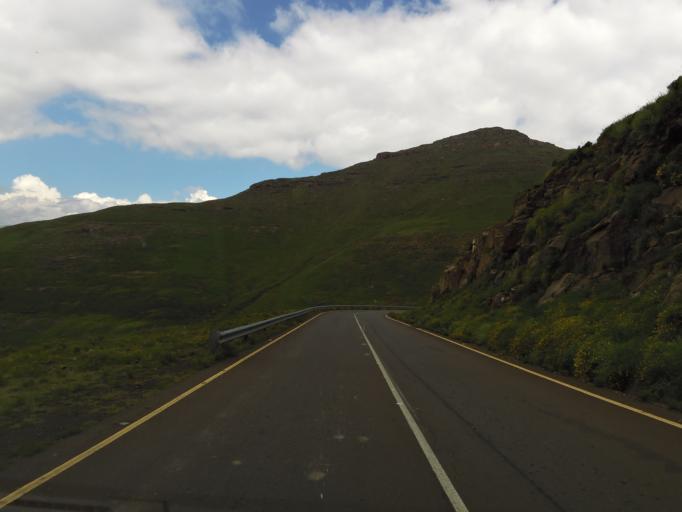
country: LS
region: Butha-Buthe
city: Butha-Buthe
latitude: -29.1156
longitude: 28.4397
